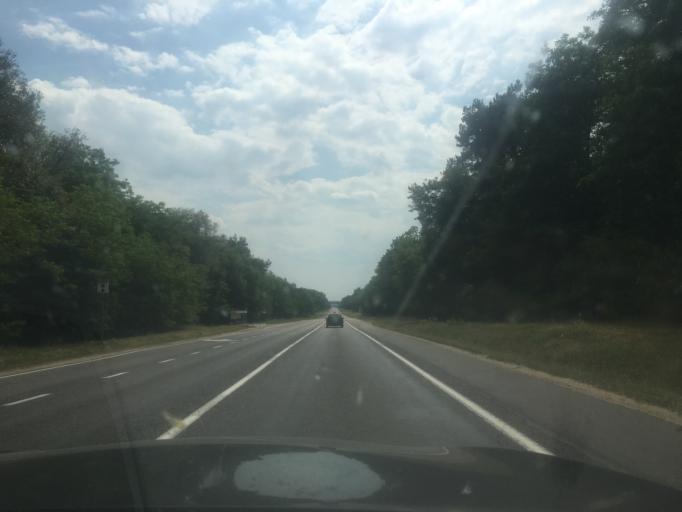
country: BY
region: Brest
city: Charnawchytsy
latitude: 52.1690
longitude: 23.7062
